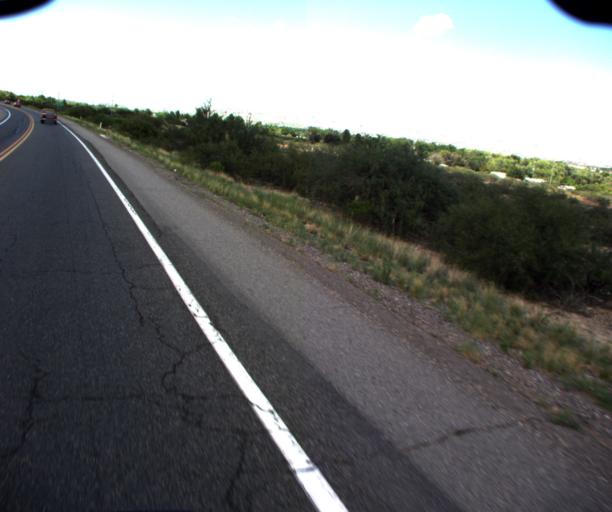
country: US
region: Arizona
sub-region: Yavapai County
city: Camp Verde
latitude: 34.5885
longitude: -111.8876
